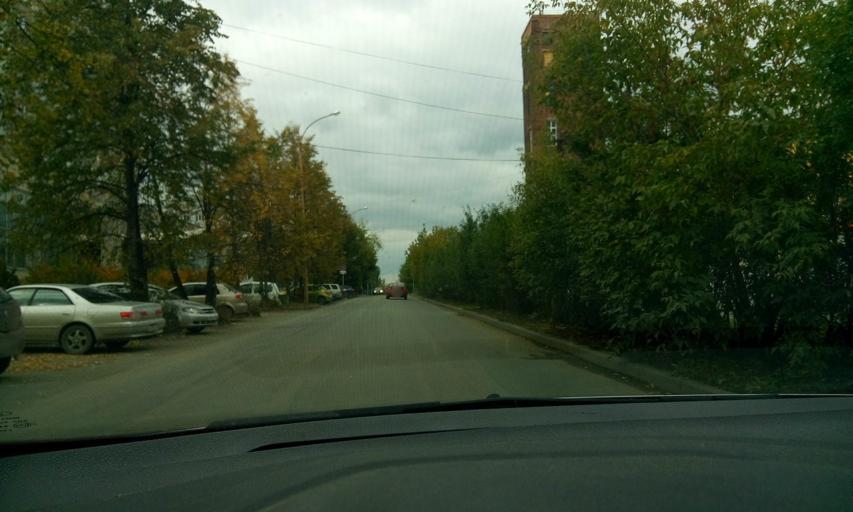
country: RU
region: Sverdlovsk
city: Yekaterinburg
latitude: 56.8420
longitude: 60.6563
